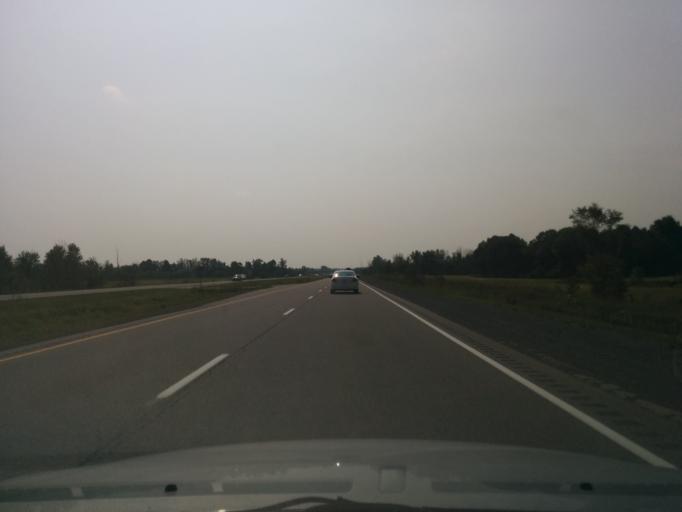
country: CA
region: Ontario
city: Bells Corners
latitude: 45.1549
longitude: -75.6845
